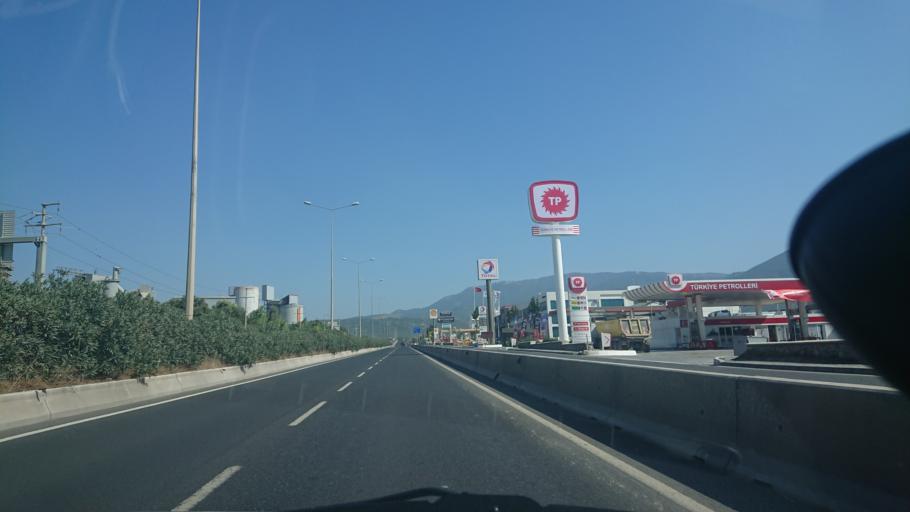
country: TR
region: Izmir
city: Bornova
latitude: 38.4550
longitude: 27.2587
